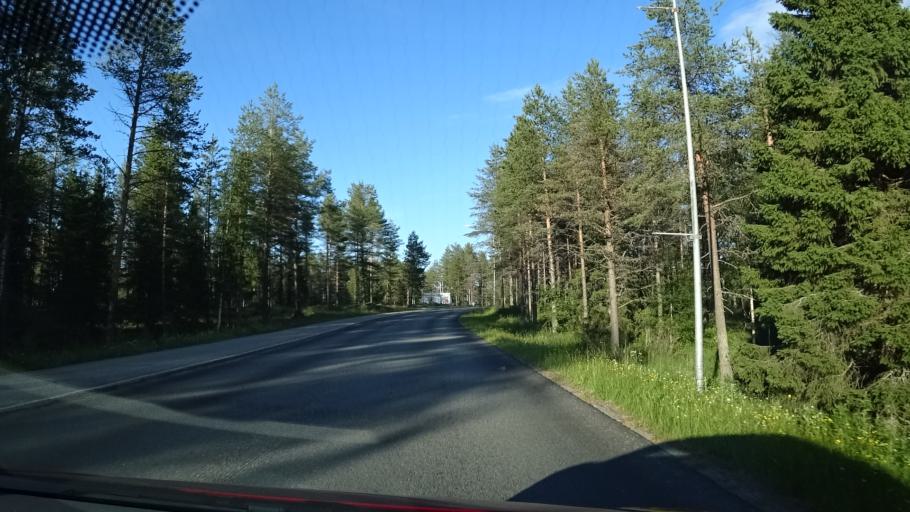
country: FI
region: Northern Ostrobothnia
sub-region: Koillismaa
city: Kuusamo
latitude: 65.9999
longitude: 29.1534
